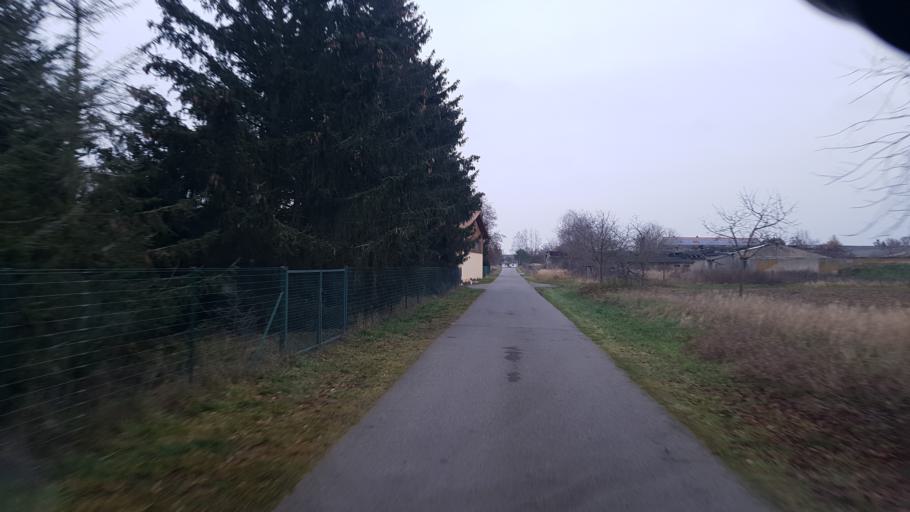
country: DE
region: Brandenburg
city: Schenkendobern
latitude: 51.9331
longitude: 14.5615
